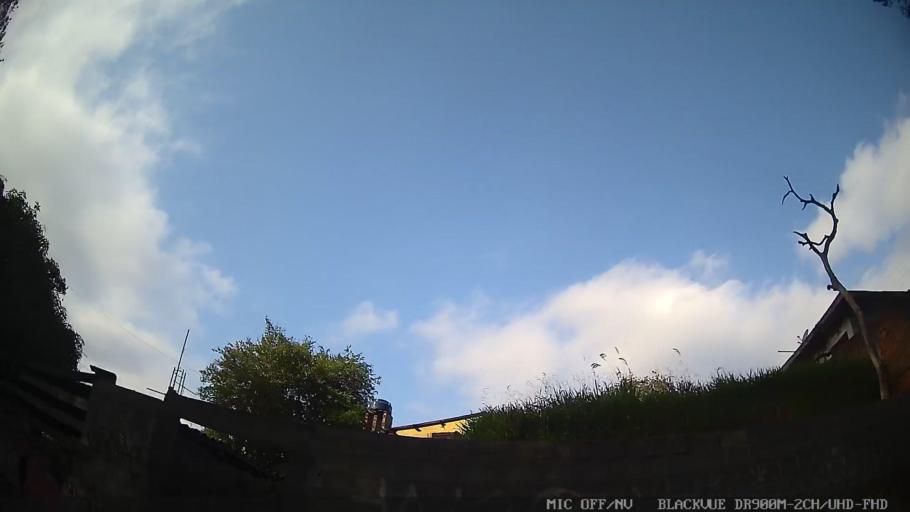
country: BR
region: Sao Paulo
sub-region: Taboao Da Serra
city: Taboao da Serra
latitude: -23.6435
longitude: -46.7649
